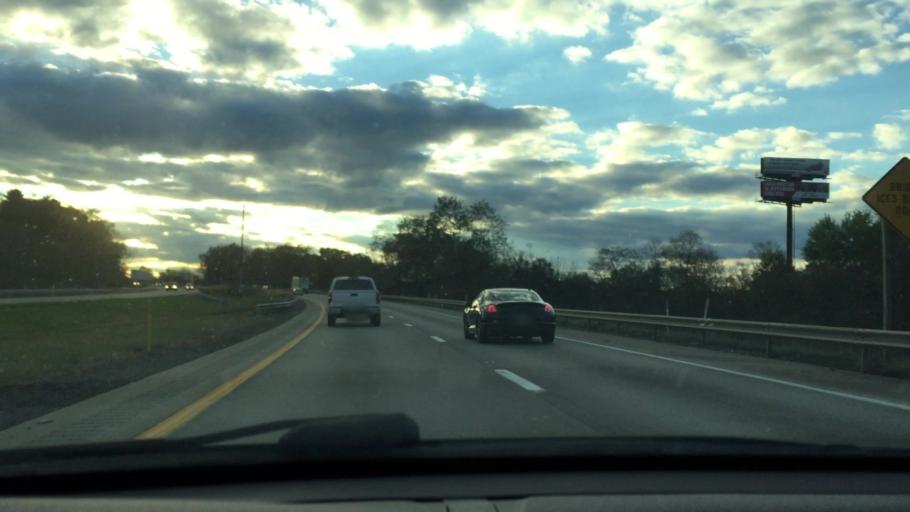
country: US
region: Pennsylvania
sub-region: Washington County
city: McGovern
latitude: 40.2111
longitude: -80.2369
